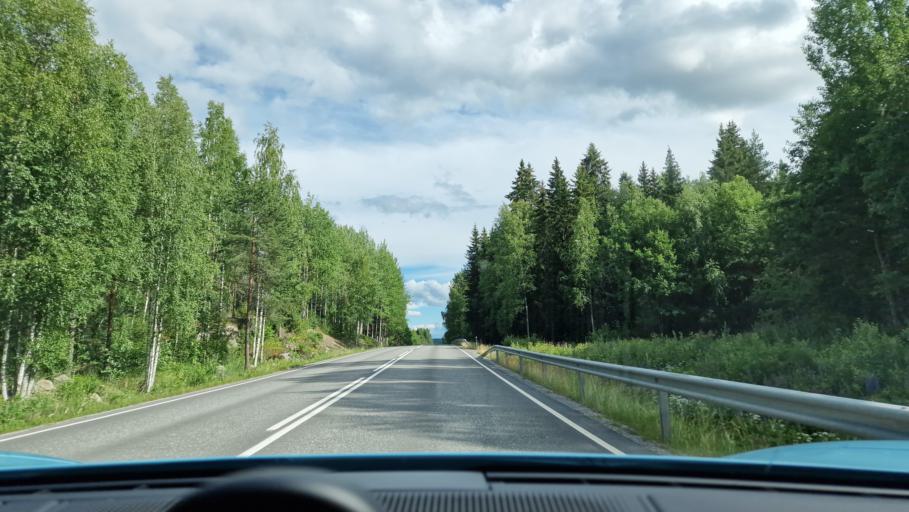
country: FI
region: Pirkanmaa
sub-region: Tampere
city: Orivesi
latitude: 61.6170
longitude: 24.3000
